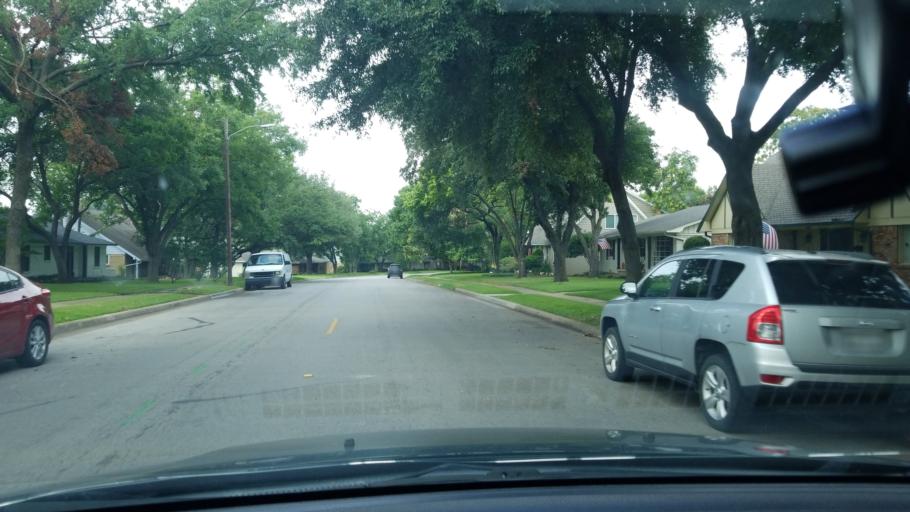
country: US
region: Texas
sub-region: Dallas County
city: Highland Park
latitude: 32.8208
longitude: -96.6949
